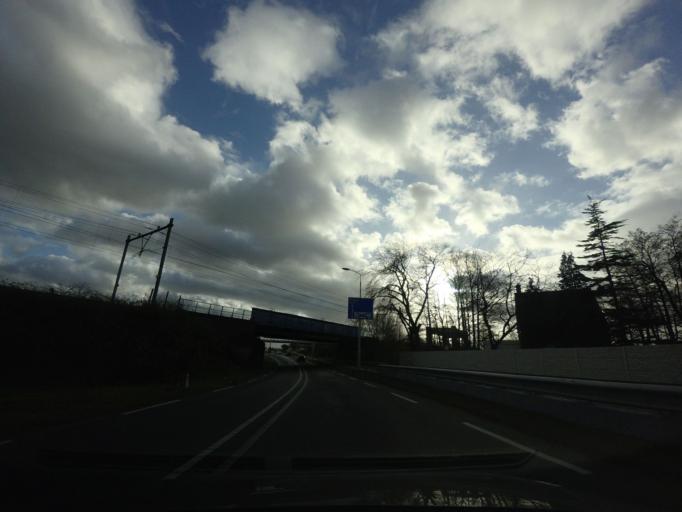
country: NL
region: North Holland
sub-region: Gemeente Langedijk
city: Broek op Langedijk
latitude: 52.6610
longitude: 4.8020
